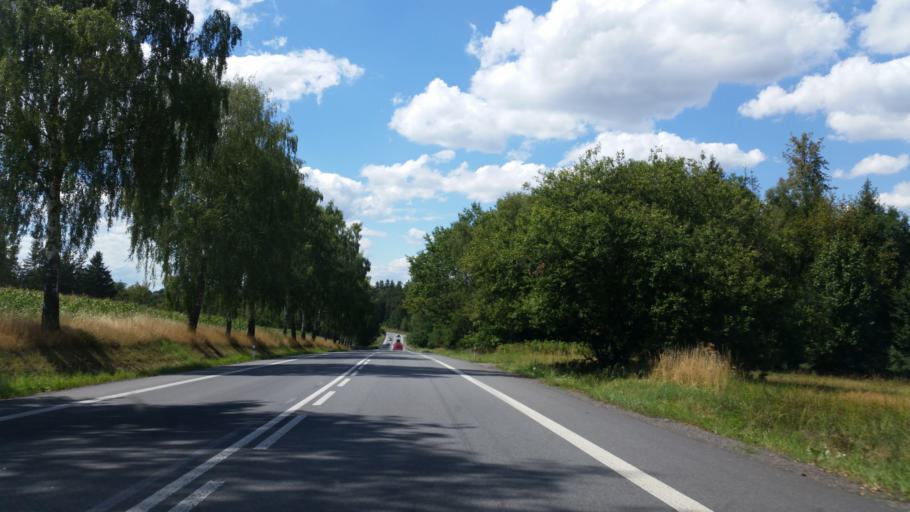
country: CZ
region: Vysocina
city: Pacov
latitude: 49.4252
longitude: 15.0387
